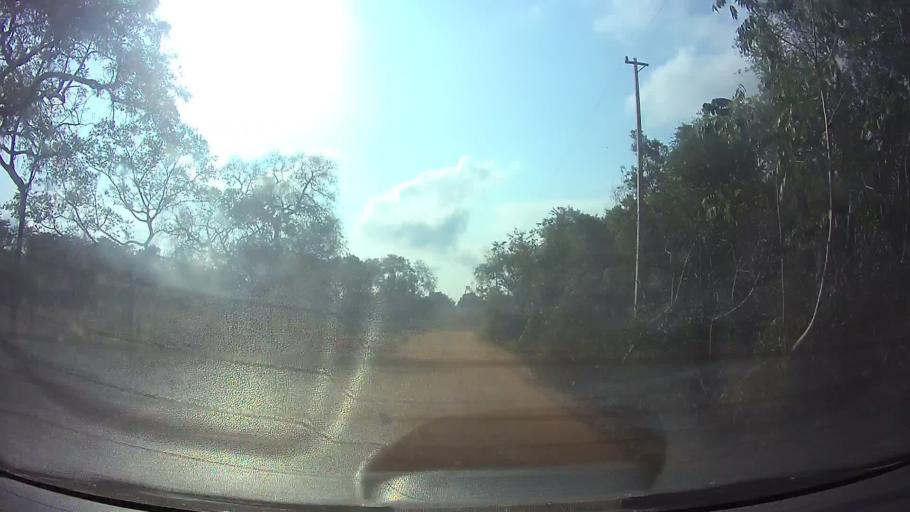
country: PY
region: Cordillera
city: Arroyos y Esteros
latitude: -25.0457
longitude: -57.1882
